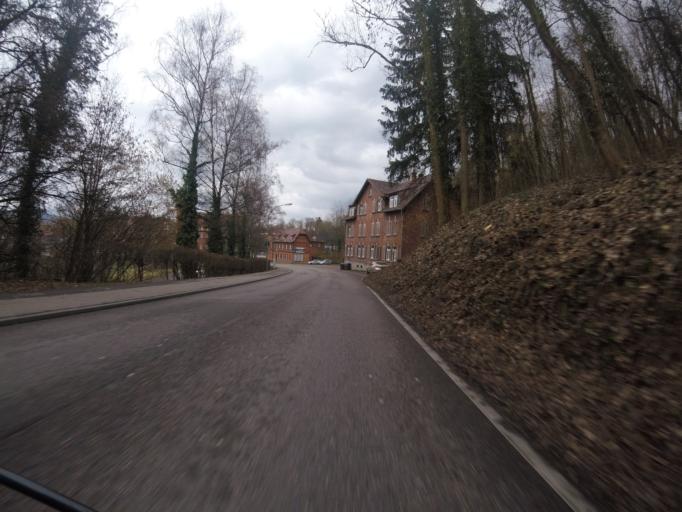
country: DE
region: Baden-Wuerttemberg
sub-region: Regierungsbezirk Stuttgart
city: Backnang
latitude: 48.9467
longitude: 9.4434
